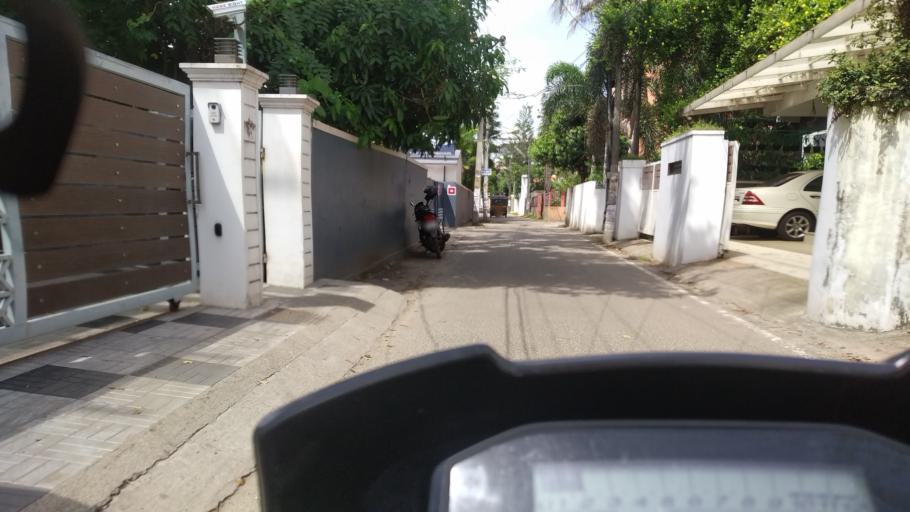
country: IN
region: Kerala
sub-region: Ernakulam
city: Cochin
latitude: 9.9875
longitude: 76.2927
